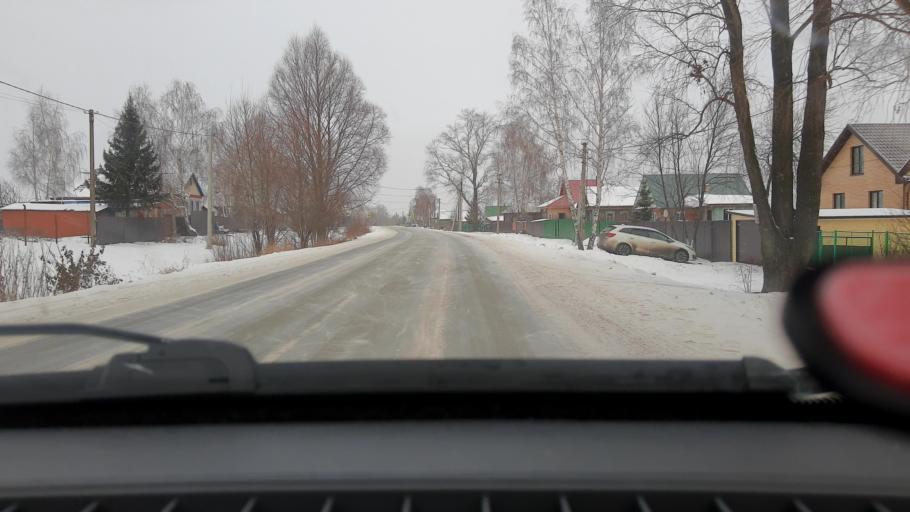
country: RU
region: Bashkortostan
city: Iglino
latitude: 54.7352
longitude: 56.3964
